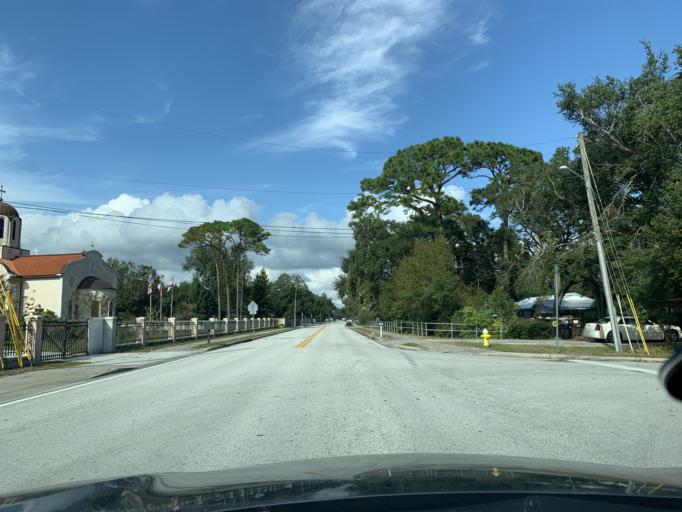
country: US
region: Florida
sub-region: Pinellas County
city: South Highpoint
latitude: 27.9104
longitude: -82.7130
